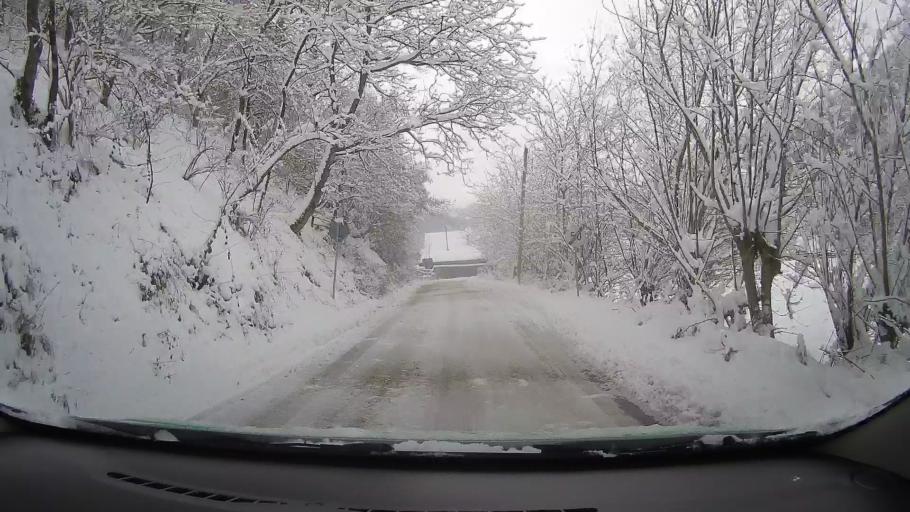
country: RO
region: Alba
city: Pianu de Sus
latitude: 45.8624
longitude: 23.4985
